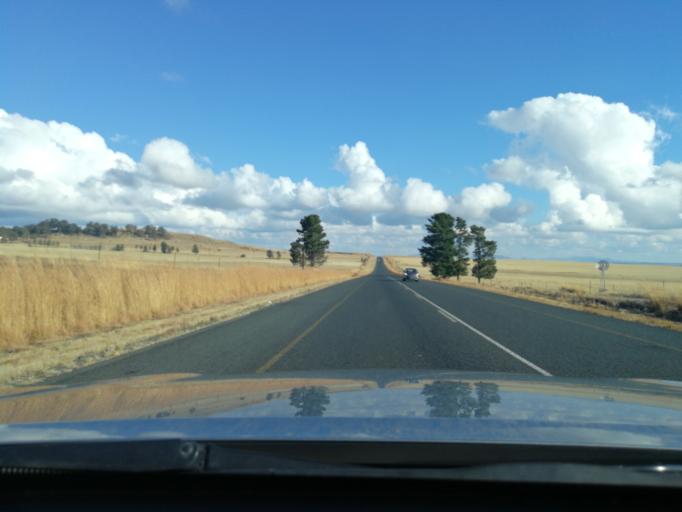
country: ZA
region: Orange Free State
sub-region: Thabo Mofutsanyana District Municipality
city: Bethlehem
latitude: -28.0731
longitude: 28.3595
